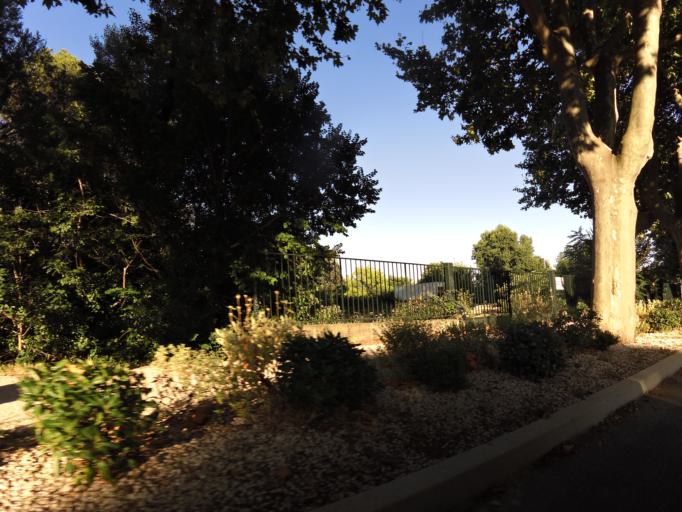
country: FR
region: Languedoc-Roussillon
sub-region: Departement du Gard
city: Remoulins
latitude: 43.9382
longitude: 4.5548
